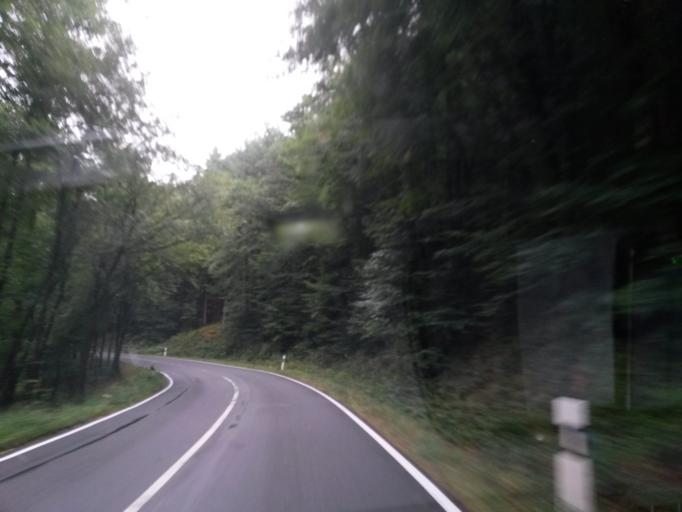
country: DE
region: North Rhine-Westphalia
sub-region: Regierungsbezirk Koln
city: Ruppichteroth
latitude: 50.8614
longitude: 7.5125
